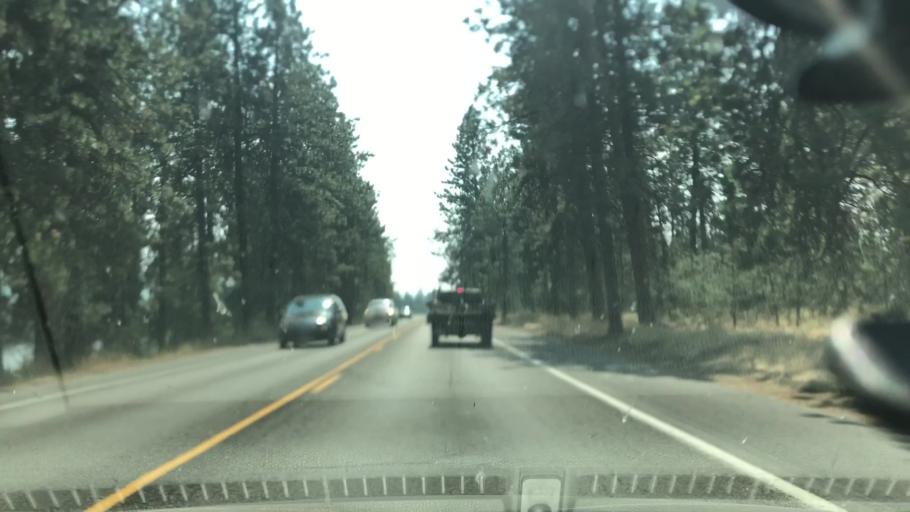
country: US
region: Washington
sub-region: Spokane County
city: Millwood
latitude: 47.6907
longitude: -117.3188
